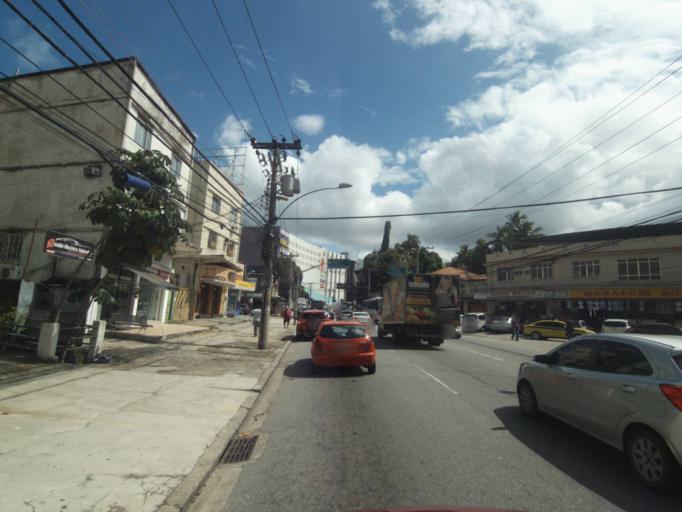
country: BR
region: Rio de Janeiro
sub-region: Sao Joao De Meriti
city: Sao Joao de Meriti
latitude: -22.9248
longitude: -43.3590
